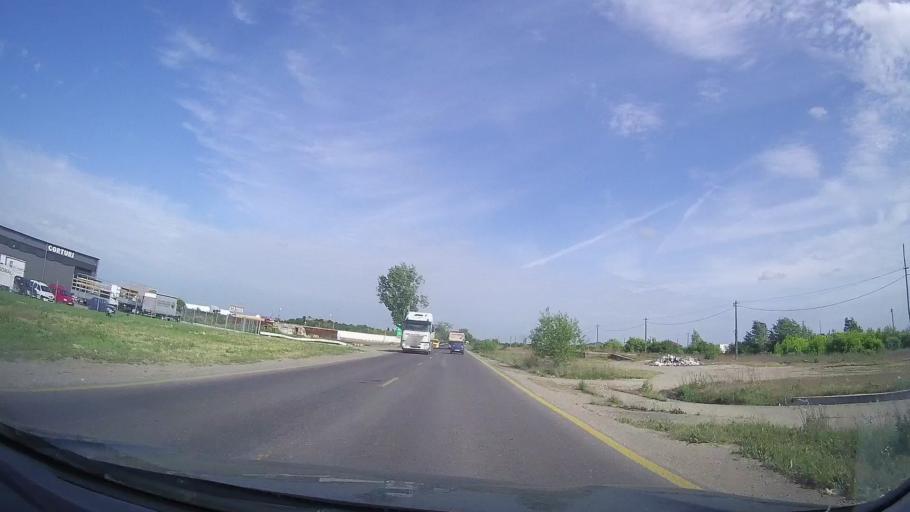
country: RO
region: Ilfov
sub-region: Comuna Magurele
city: Varteju
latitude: 44.3707
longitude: 26.0116
